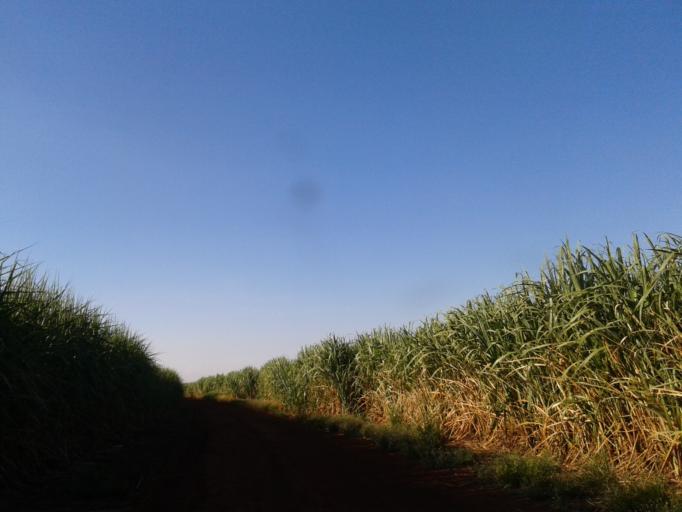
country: BR
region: Minas Gerais
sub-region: Centralina
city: Centralina
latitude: -18.6640
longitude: -49.2708
